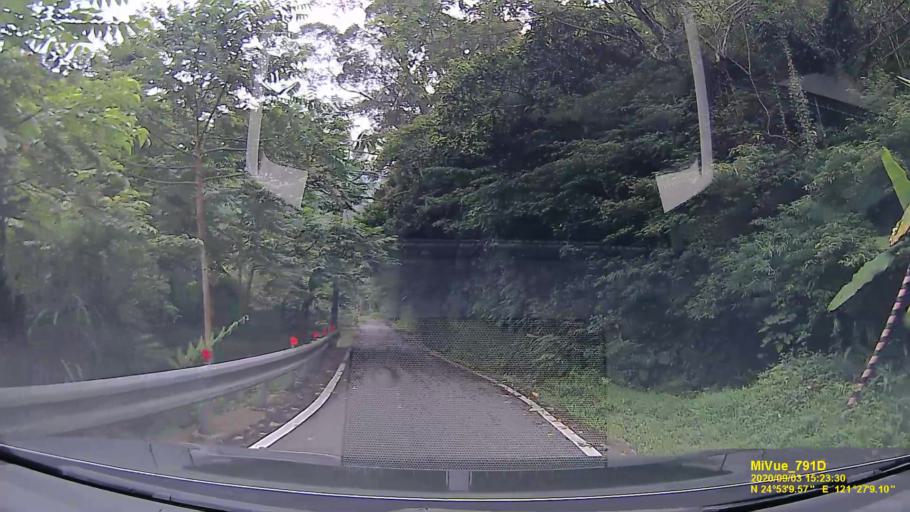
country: TW
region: Taipei
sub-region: Taipei
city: Banqiao
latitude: 24.8860
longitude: 121.4526
